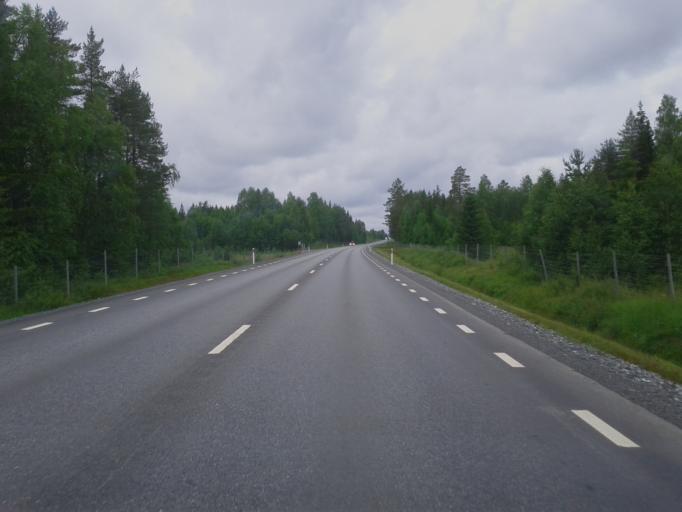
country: SE
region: Vaesterbotten
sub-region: Skelleftea Kommun
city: Forsbacka
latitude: 64.8424
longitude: 20.5053
